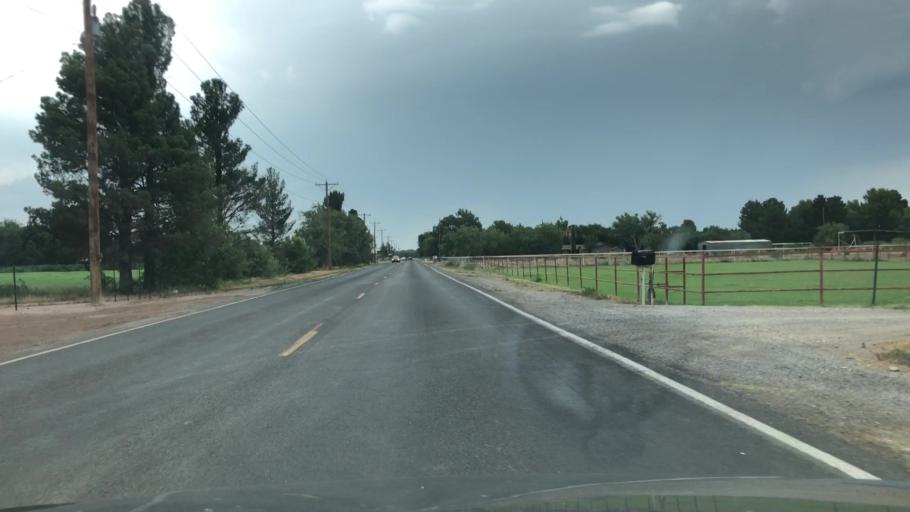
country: US
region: Texas
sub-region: El Paso County
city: Canutillo
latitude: 31.9238
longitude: -106.6275
